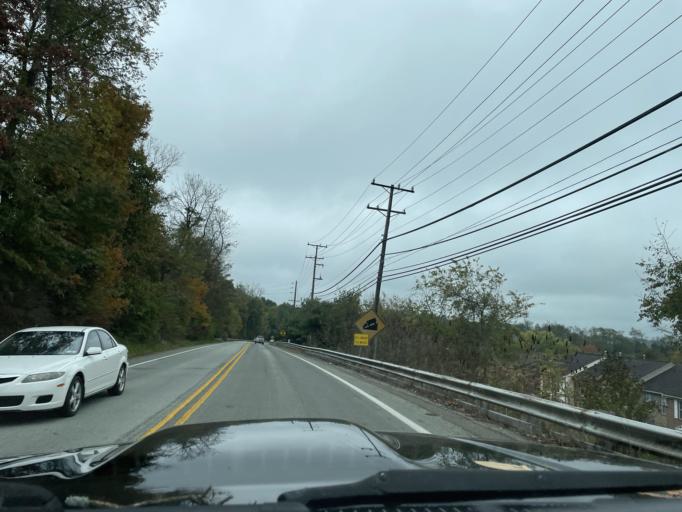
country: US
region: Pennsylvania
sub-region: Allegheny County
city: Springdale
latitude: 40.5298
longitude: -79.7788
